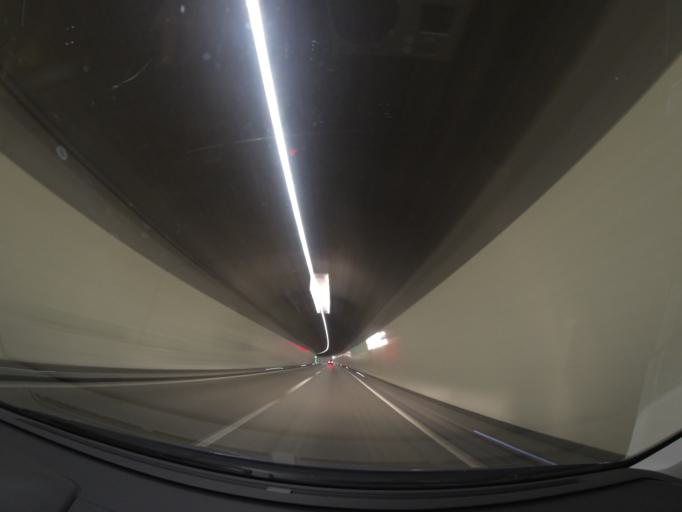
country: CH
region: Saint Gallen
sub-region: Wahlkreis Sarganserland
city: Quarten
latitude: 47.1097
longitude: 9.2384
